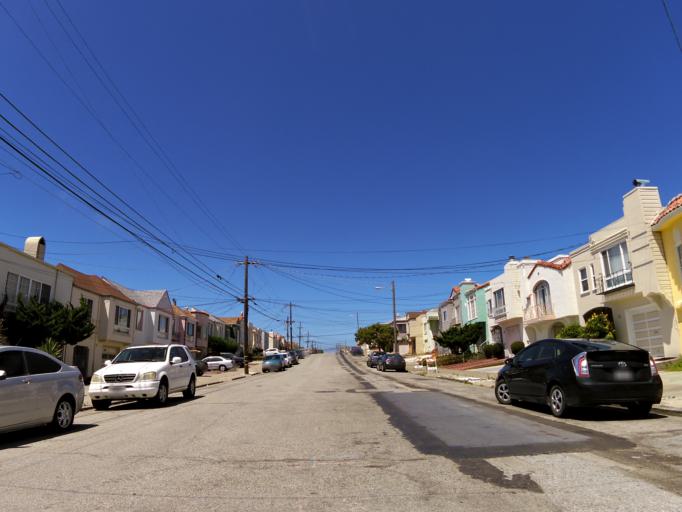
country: US
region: California
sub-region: San Mateo County
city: Daly City
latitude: 37.7451
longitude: -122.4877
